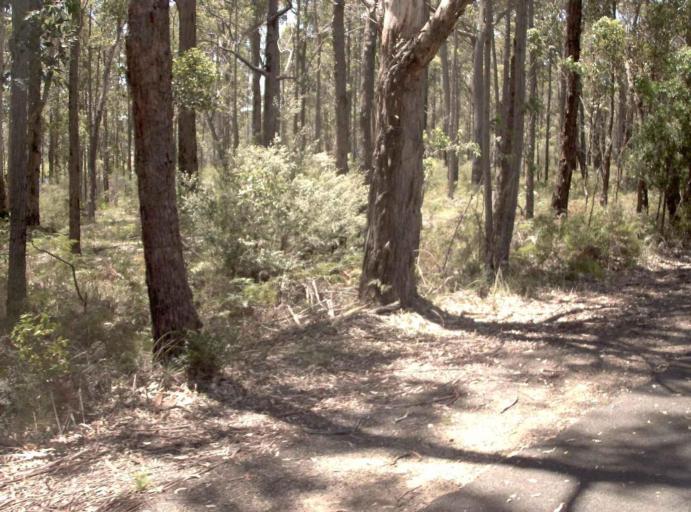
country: AU
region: Victoria
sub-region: East Gippsland
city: Lakes Entrance
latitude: -37.7438
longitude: 148.1635
